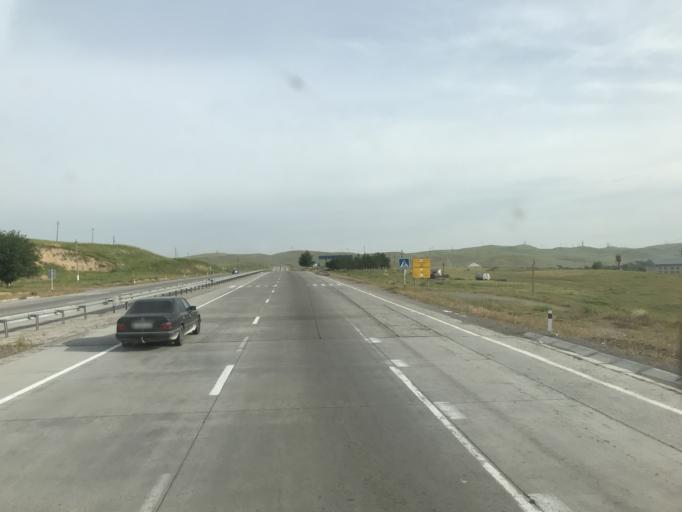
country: KZ
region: Ongtustik Qazaqstan
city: Qazyqurt
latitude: 41.9740
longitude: 69.4977
